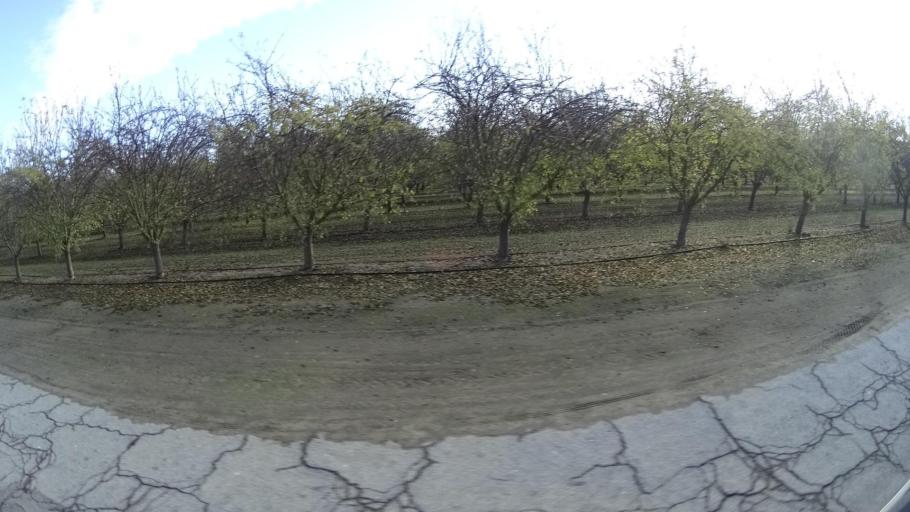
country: US
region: California
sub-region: Kern County
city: Delano
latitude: 35.7147
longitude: -119.3208
